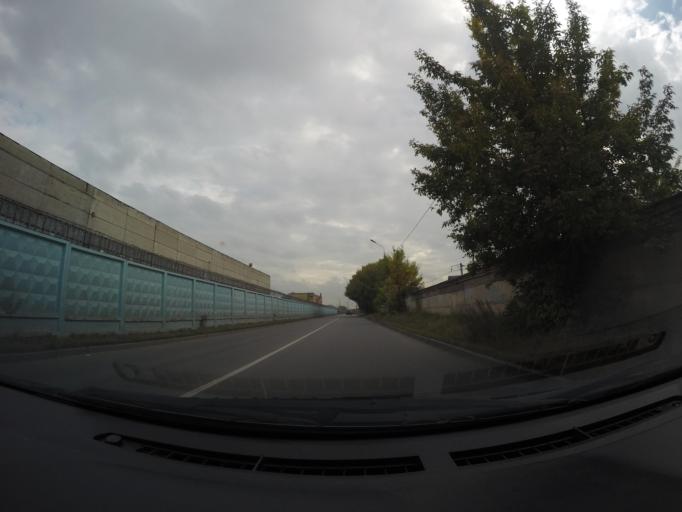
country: RU
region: Moscow
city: Lefortovo
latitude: 55.7685
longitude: 37.7208
